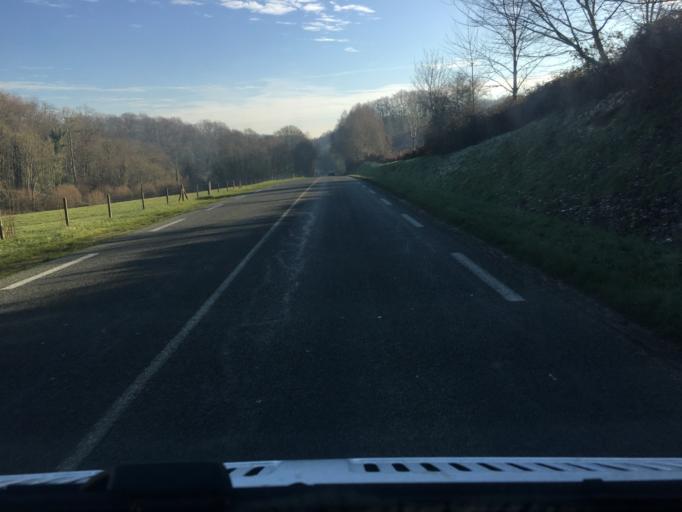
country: FR
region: Haute-Normandie
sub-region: Departement de la Seine-Maritime
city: Yvetot
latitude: 49.6059
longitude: 0.7486
